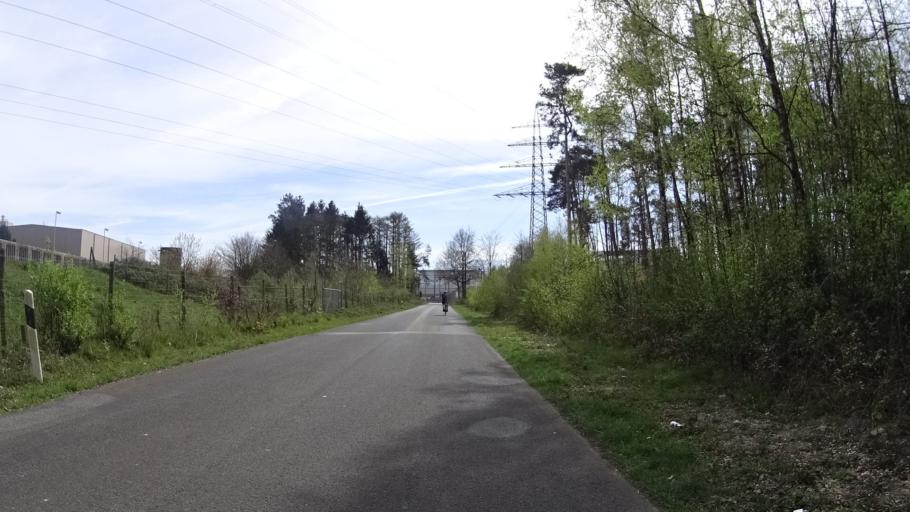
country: DE
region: Lower Saxony
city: Lingen
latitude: 52.4712
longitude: 7.3154
